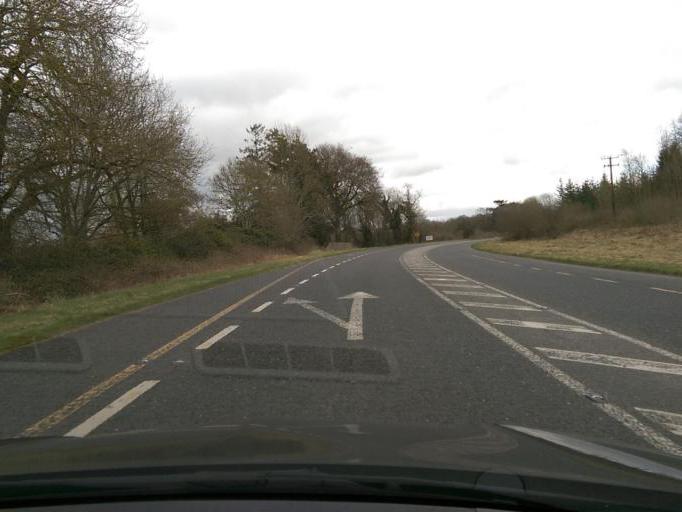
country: IE
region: Leinster
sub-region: An Iarmhi
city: Athlone
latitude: 53.4010
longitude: -7.8640
